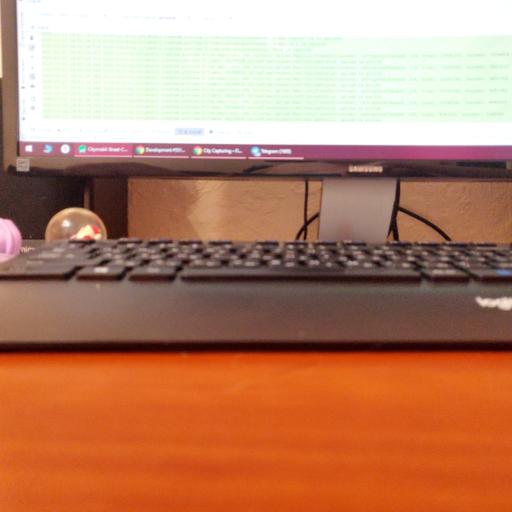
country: FI
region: Varsinais-Suomi
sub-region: Salo
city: Kuusjoki
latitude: 60.6235
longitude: 23.3363
